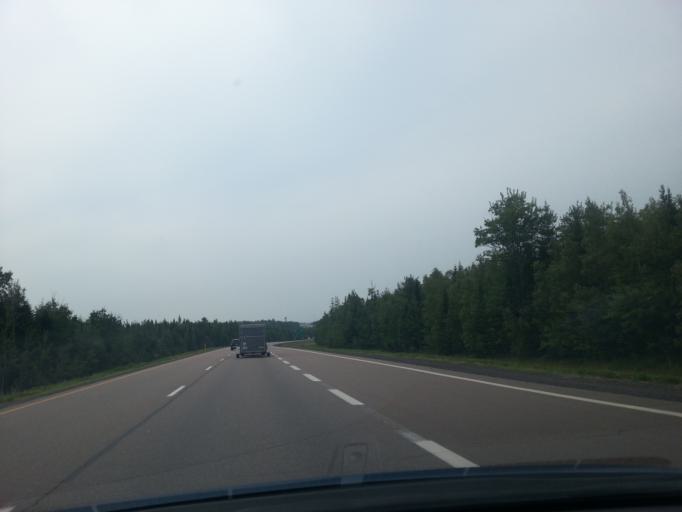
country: CA
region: New Brunswick
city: Salisbury
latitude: 46.0554
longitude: -65.0314
